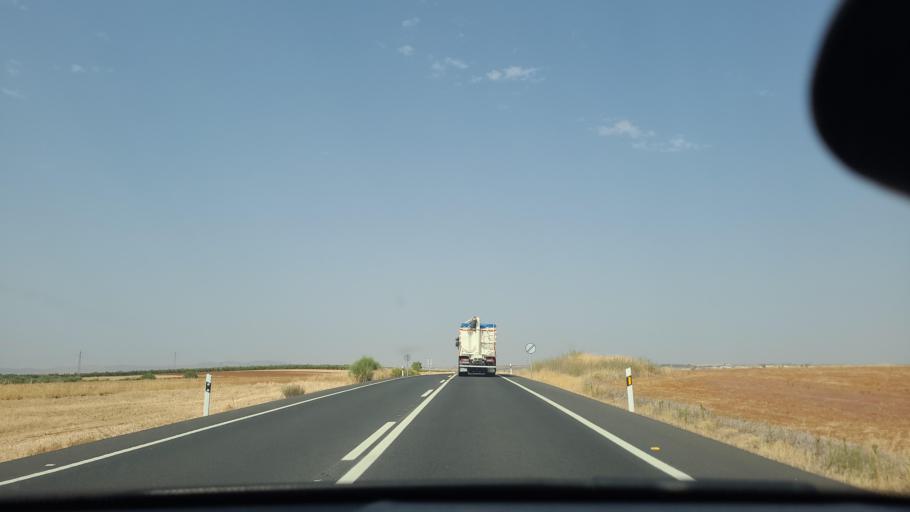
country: ES
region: Extremadura
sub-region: Provincia de Badajoz
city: Berlanga
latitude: 38.2665
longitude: -5.7753
